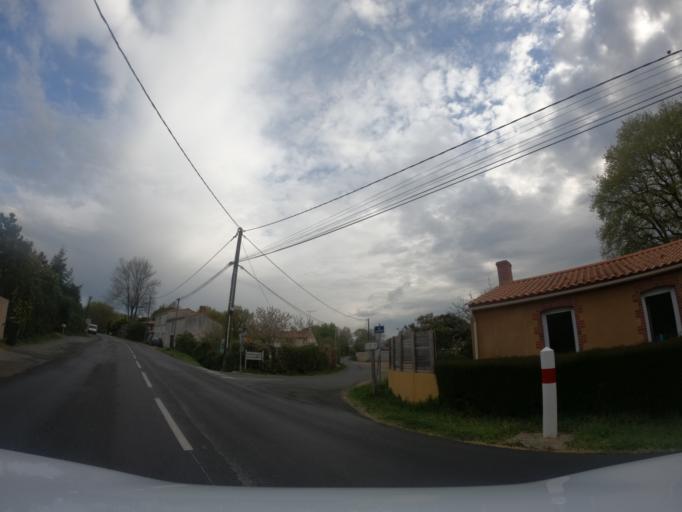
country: FR
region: Pays de la Loire
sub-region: Departement de la Vendee
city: Saint-Vincent-sur-Graon
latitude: 46.5340
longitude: -1.3679
